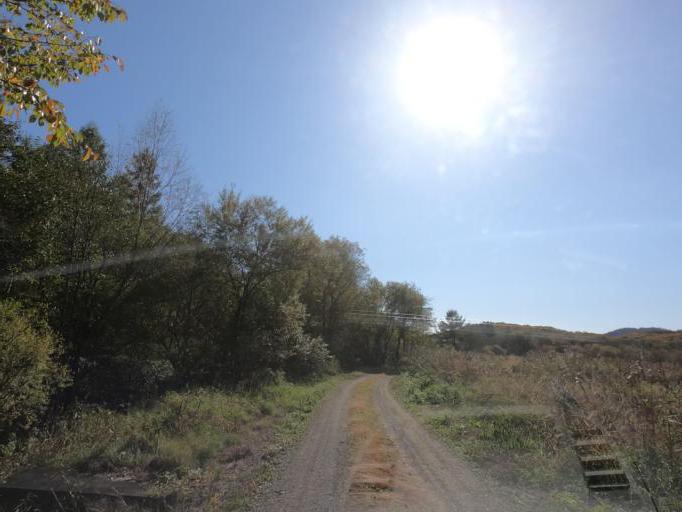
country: JP
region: Hokkaido
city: Obihiro
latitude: 42.7271
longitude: 143.4496
